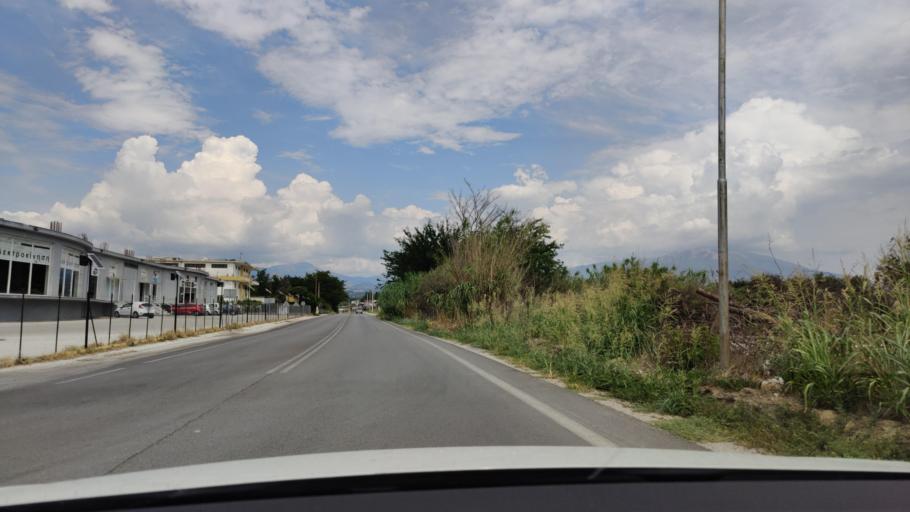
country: GR
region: Central Macedonia
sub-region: Nomos Serron
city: Serres
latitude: 41.0610
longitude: 23.5388
